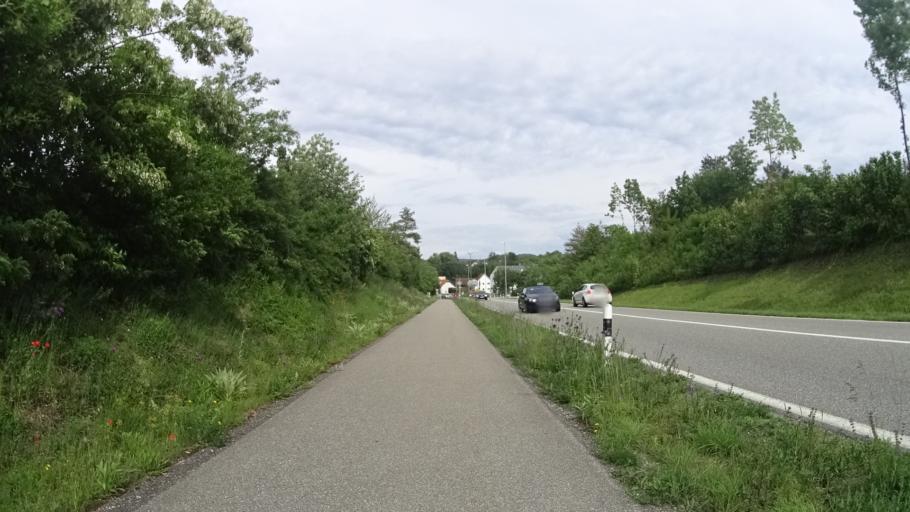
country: CH
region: Aargau
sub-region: Bezirk Laufenburg
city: Eiken
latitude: 47.5519
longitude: 7.9820
